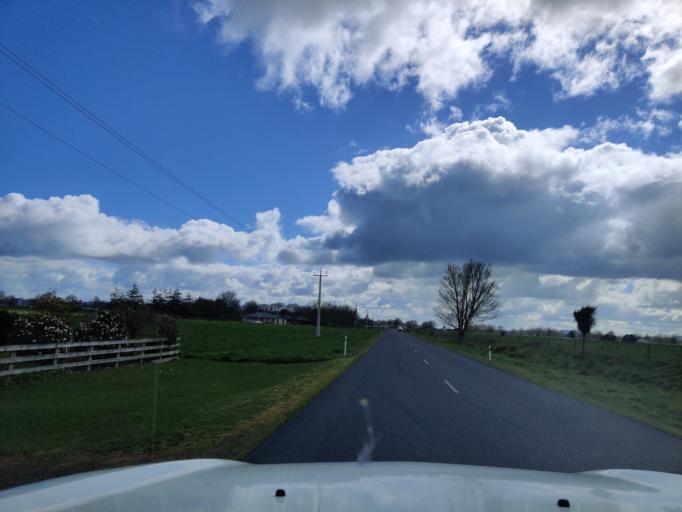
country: NZ
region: Waikato
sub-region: Hamilton City
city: Hamilton
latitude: -37.6206
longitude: 175.3193
